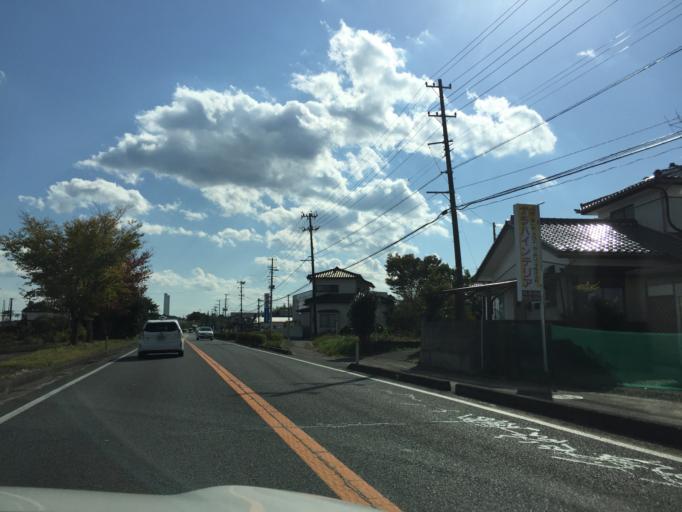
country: JP
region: Fukushima
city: Namie
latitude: 37.2643
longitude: 140.9965
